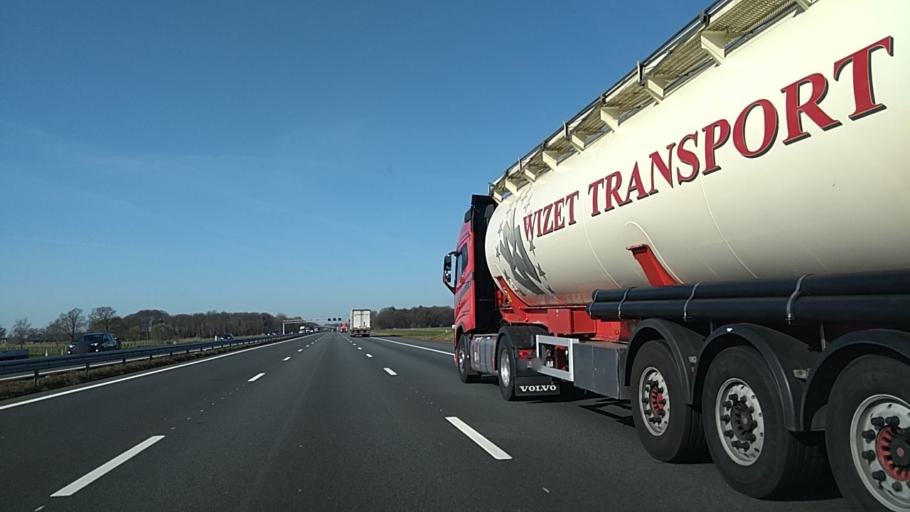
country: NL
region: Gelderland
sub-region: Gemeente Lochem
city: Harfsen
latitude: 52.2424
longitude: 6.2724
